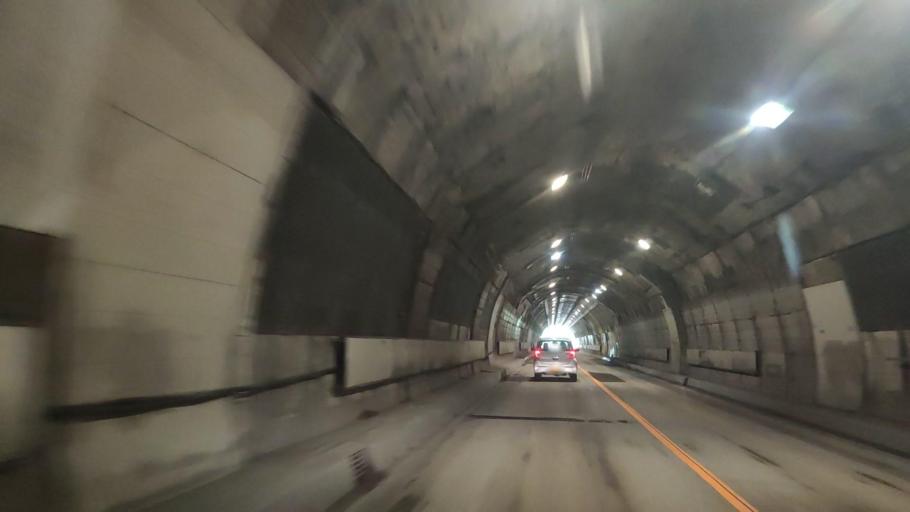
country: JP
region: Hokkaido
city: Date
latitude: 42.5711
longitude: 140.7333
